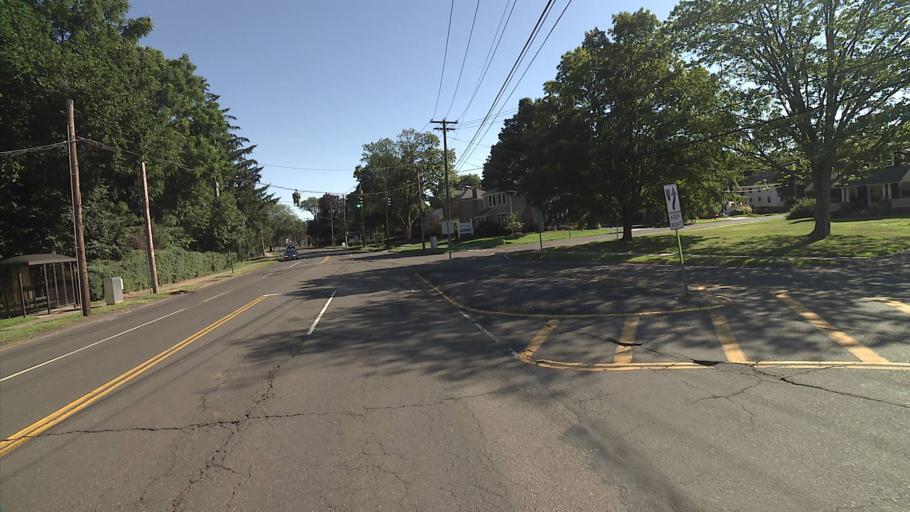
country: US
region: Connecticut
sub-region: New Haven County
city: Hamden
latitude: 41.3919
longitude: -72.8977
